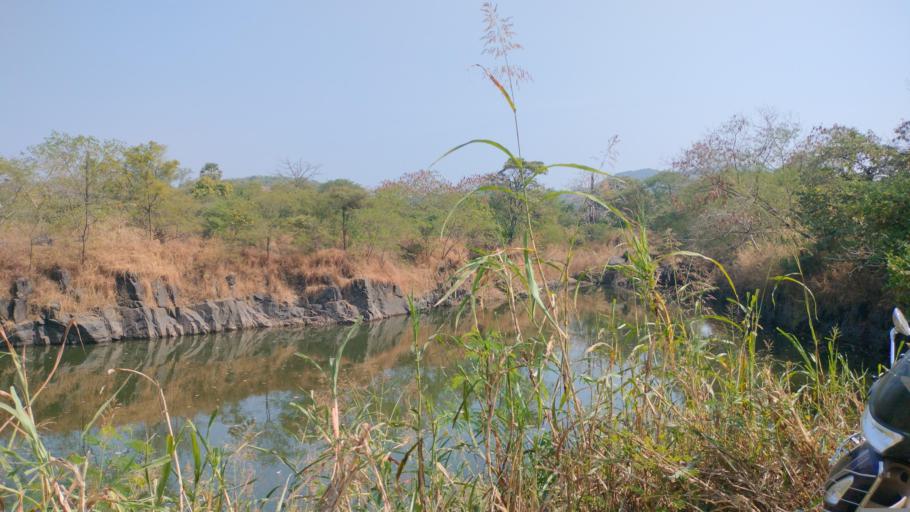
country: IN
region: Maharashtra
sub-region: Thane
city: Bhayandar
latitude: 19.3758
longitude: 72.8626
